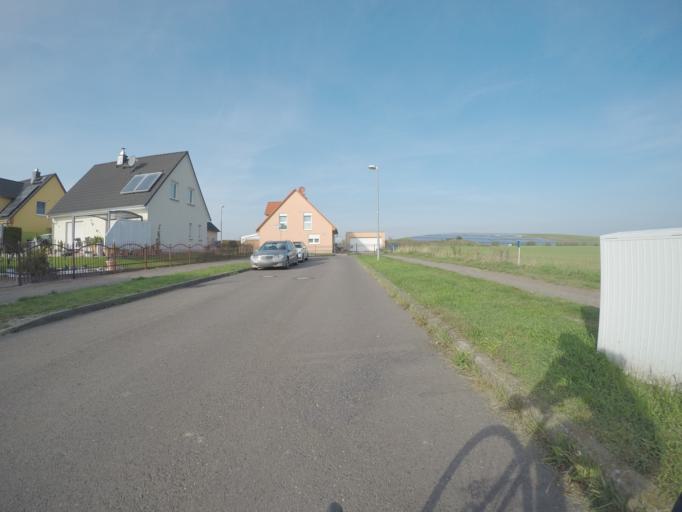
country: DE
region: Berlin
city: Gropiusstadt
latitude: 52.4032
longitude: 13.4544
